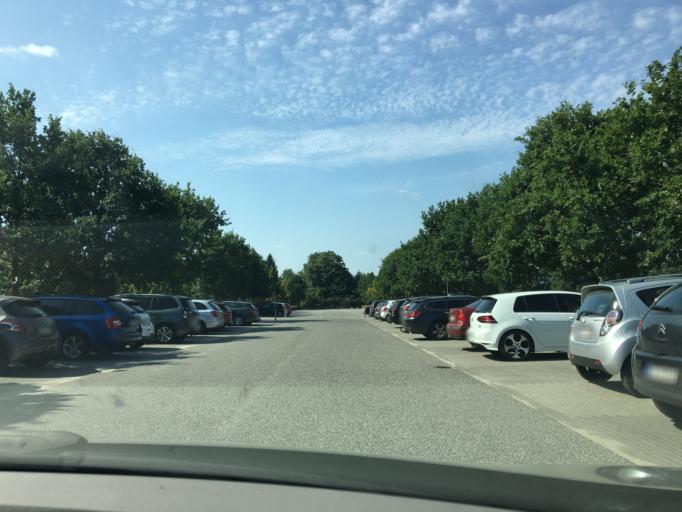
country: DK
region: South Denmark
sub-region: Odense Kommune
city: Odense
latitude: 55.3798
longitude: 10.3668
